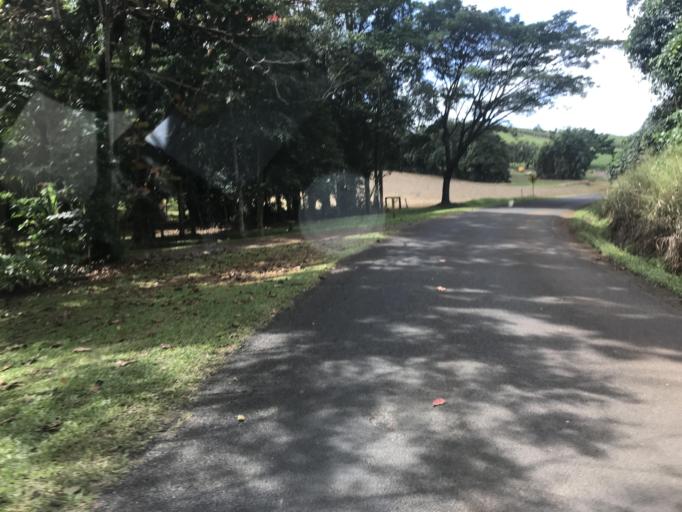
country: AU
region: Queensland
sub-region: Cassowary Coast
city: Innisfail
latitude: -17.5496
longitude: 145.8683
